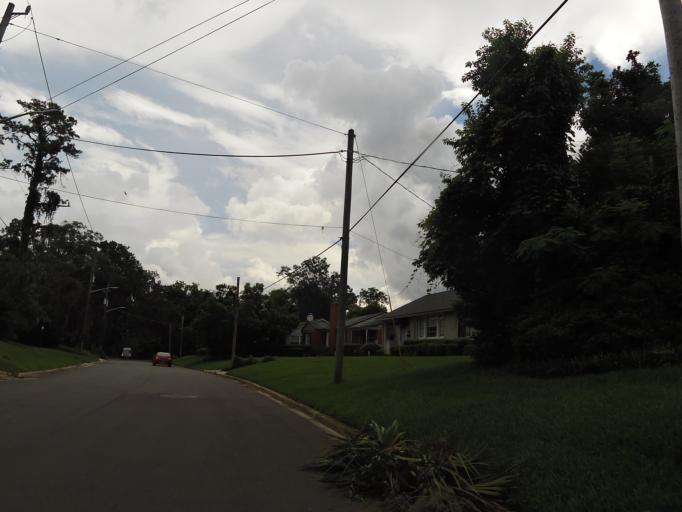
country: US
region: Florida
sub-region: Duval County
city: Jacksonville
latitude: 30.2957
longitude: -81.6456
